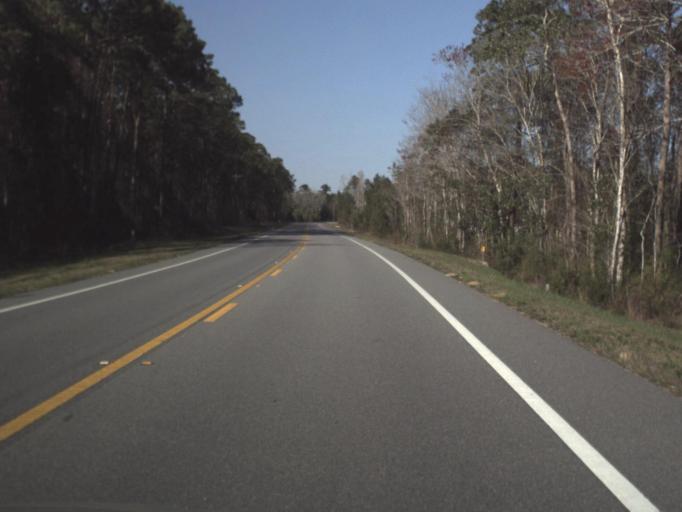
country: US
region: Florida
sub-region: Calhoun County
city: Blountstown
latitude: 30.3417
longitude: -85.2166
